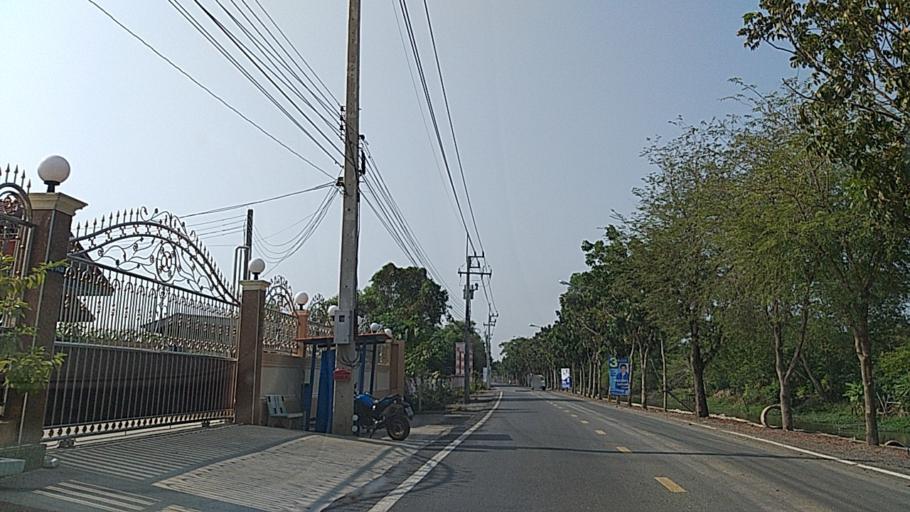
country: TH
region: Pathum Thani
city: Thanyaburi
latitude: 13.9895
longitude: 100.7059
